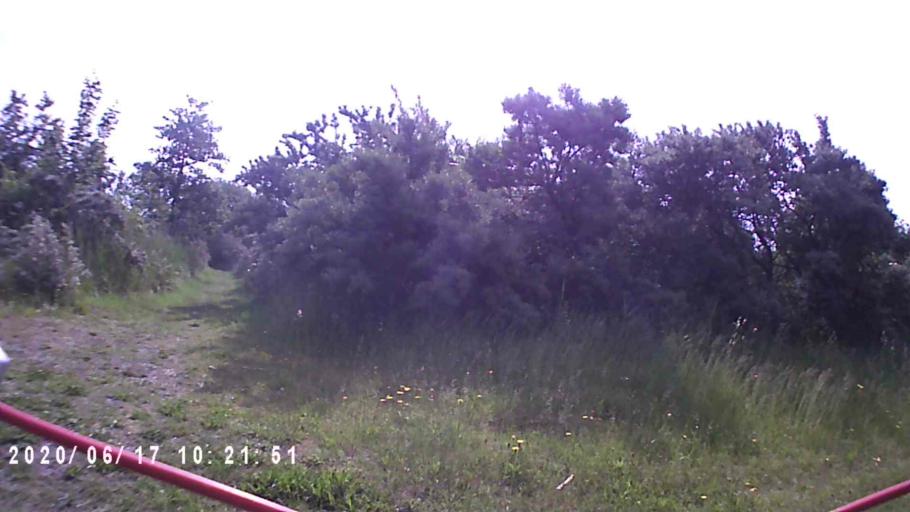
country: NL
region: Groningen
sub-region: Gemeente De Marne
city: Ulrum
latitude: 53.3907
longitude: 6.2512
